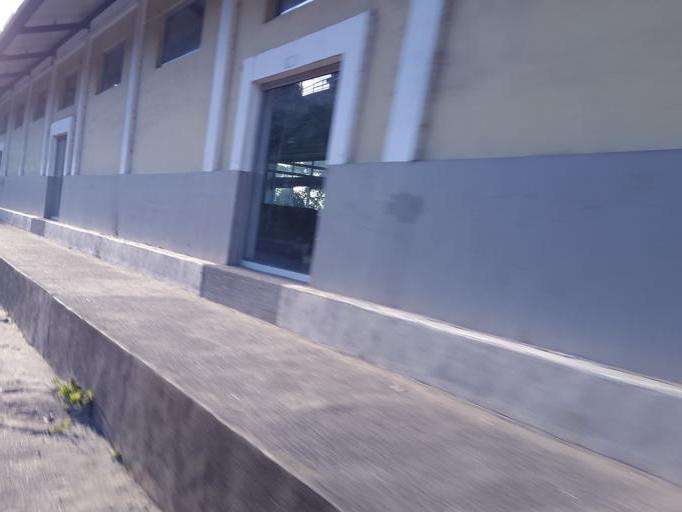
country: CO
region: Quindio
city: Armenia
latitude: 4.5325
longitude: -75.6804
